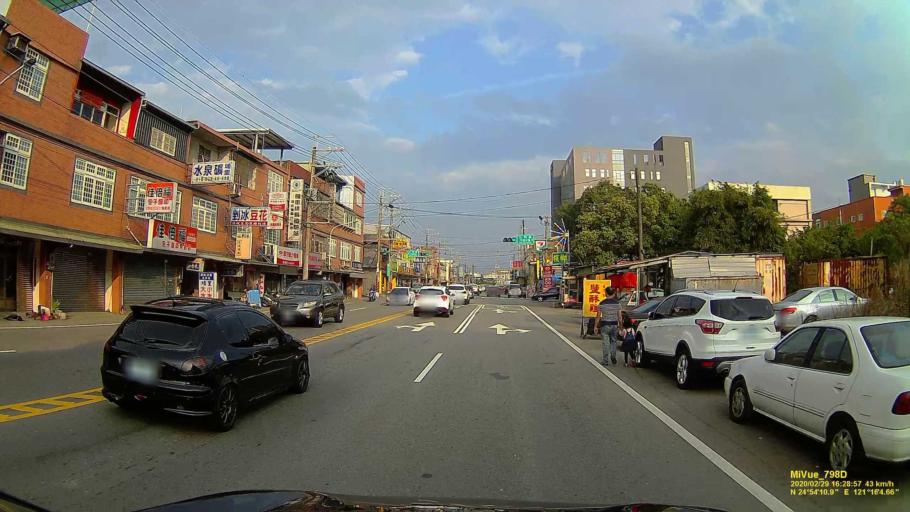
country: TW
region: Taiwan
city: Daxi
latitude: 24.9030
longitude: 121.2682
